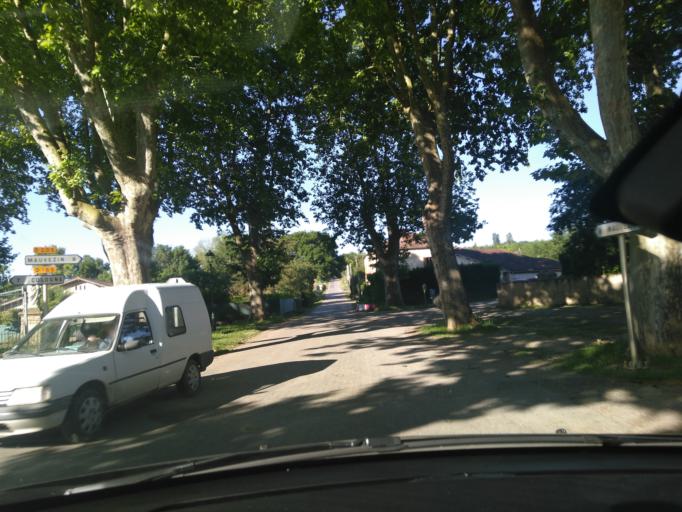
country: FR
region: Midi-Pyrenees
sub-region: Departement du Tarn-et-Garonne
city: Beaumont-de-Lomagne
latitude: 43.7737
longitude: 0.9291
